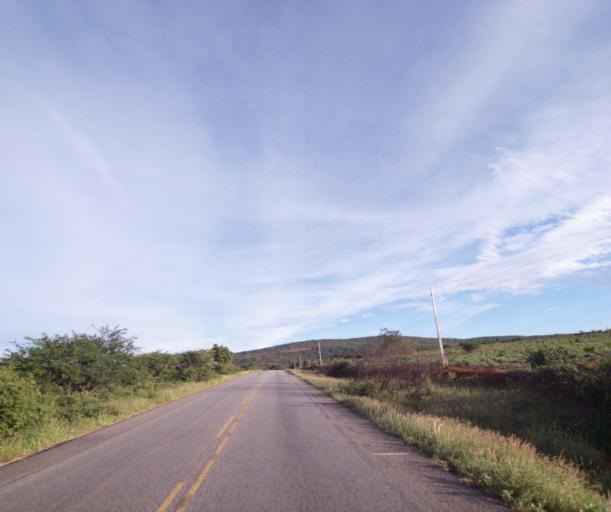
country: BR
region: Bahia
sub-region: Cacule
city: Cacule
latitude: -14.1868
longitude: -42.1613
